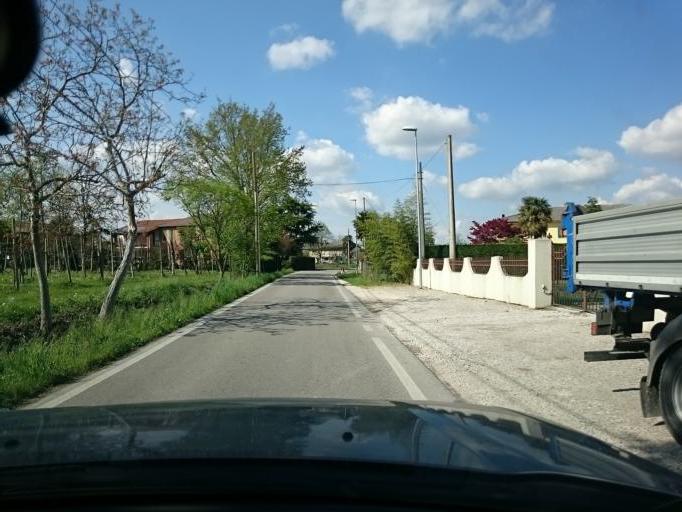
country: IT
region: Veneto
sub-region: Provincia di Padova
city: Pionca
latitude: 45.4581
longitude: 11.9758
